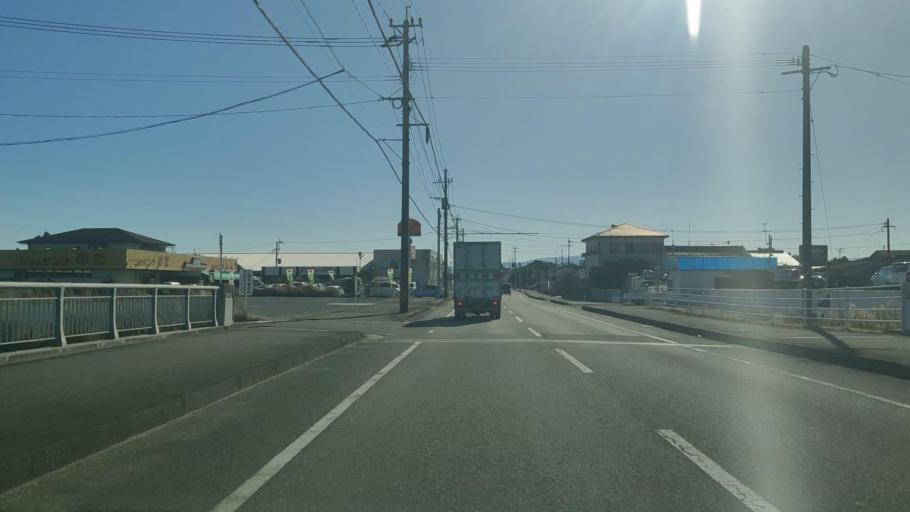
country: JP
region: Miyazaki
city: Miyazaki-shi
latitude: 31.9416
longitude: 131.4572
